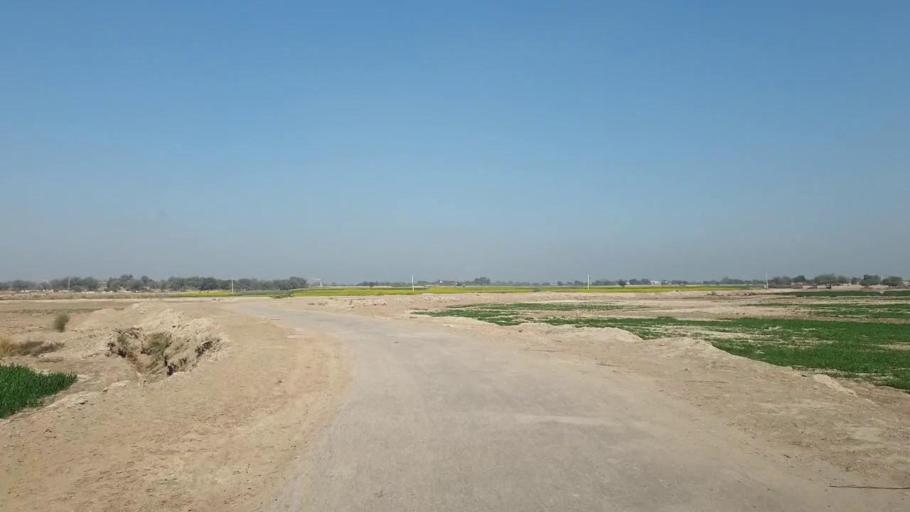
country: PK
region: Sindh
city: Shahpur Chakar
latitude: 26.1208
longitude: 68.6068
